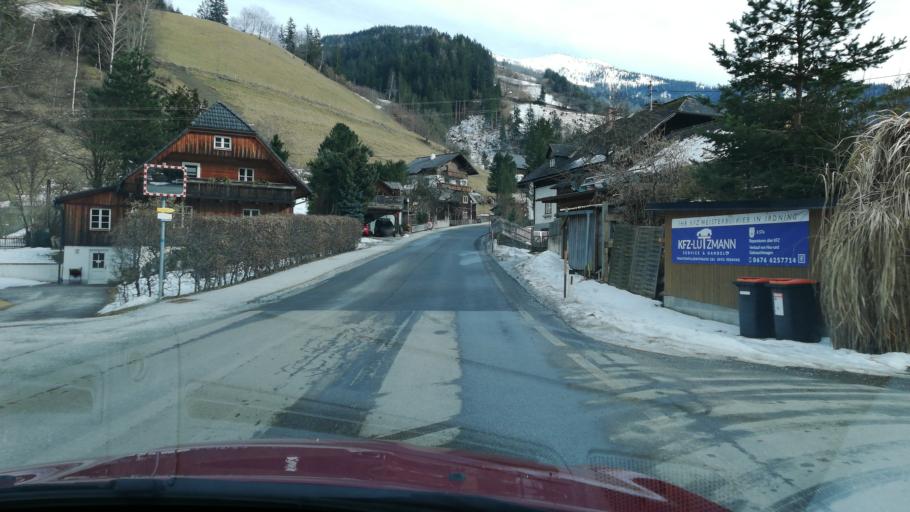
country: AT
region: Styria
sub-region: Politischer Bezirk Liezen
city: Donnersbach
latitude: 47.4637
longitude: 14.1302
